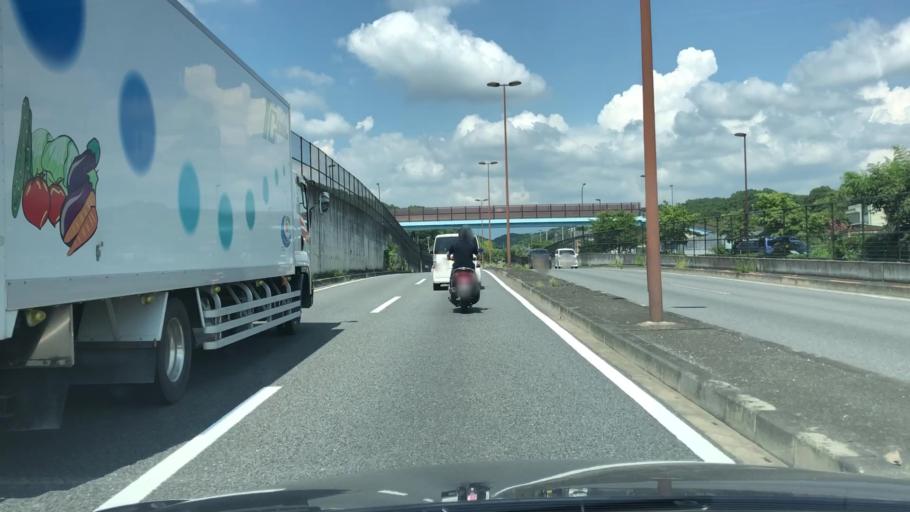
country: JP
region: Tokyo
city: Fussa
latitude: 35.7079
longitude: 139.2923
